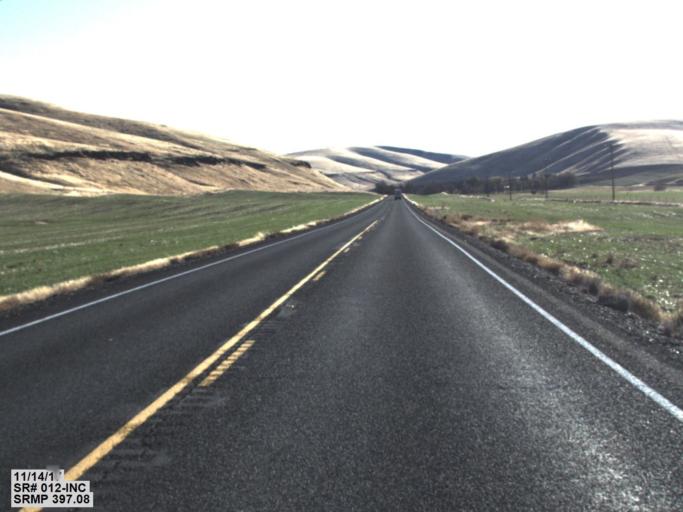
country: US
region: Washington
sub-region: Garfield County
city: Pomeroy
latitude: 46.4730
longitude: -117.7232
